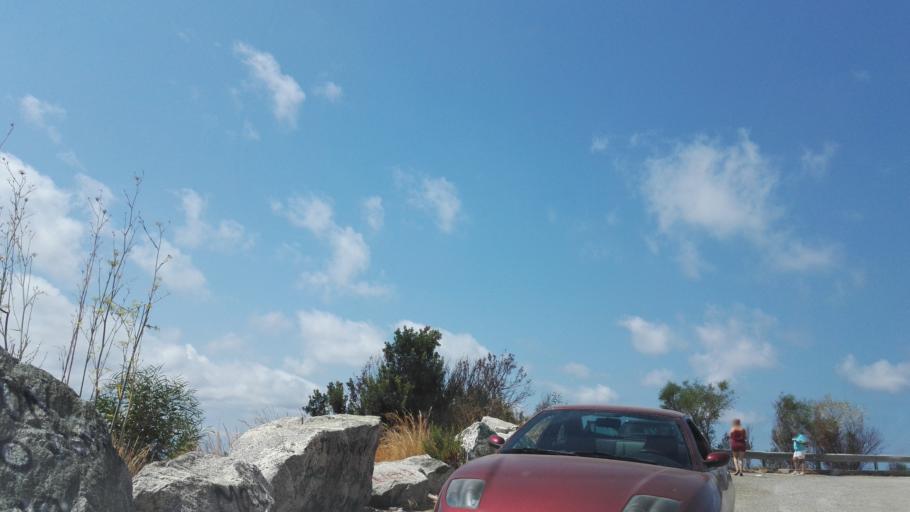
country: IT
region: Calabria
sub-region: Provincia di Vibo-Valentia
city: Joppolo
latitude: 38.5904
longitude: 15.8805
